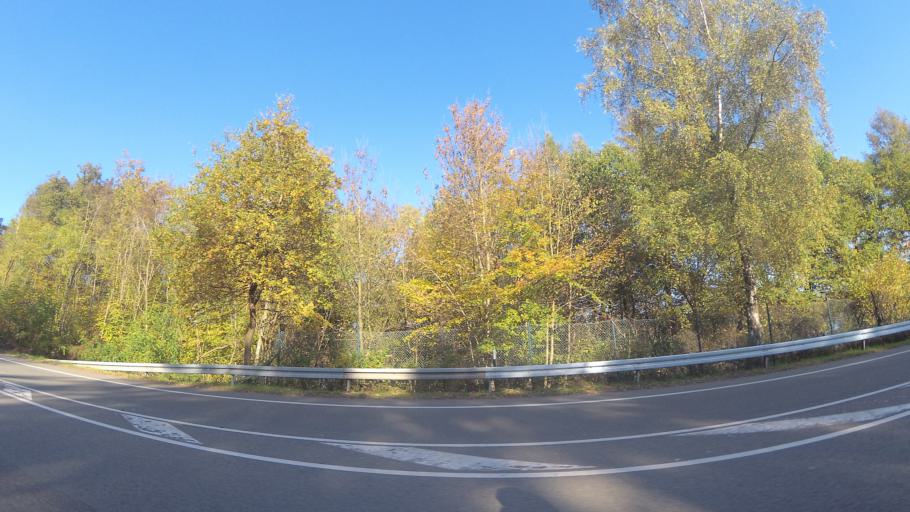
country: DE
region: Saarland
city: Losheim
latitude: 49.5180
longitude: 6.7271
